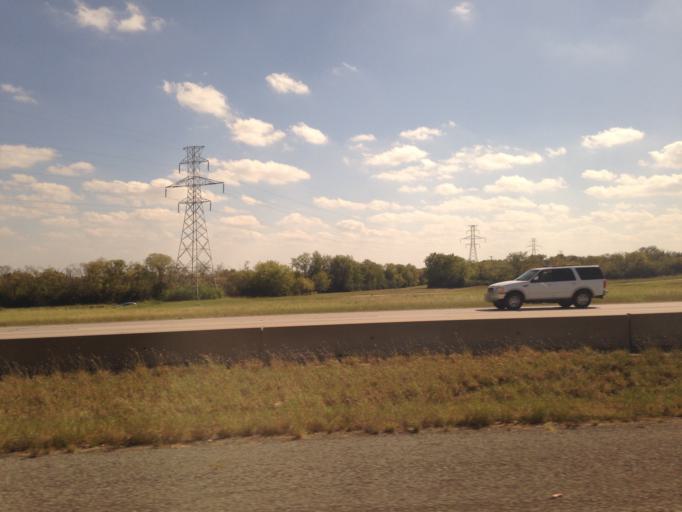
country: US
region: Texas
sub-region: Tarrant County
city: Sansom Park
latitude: 32.8291
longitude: -97.3808
